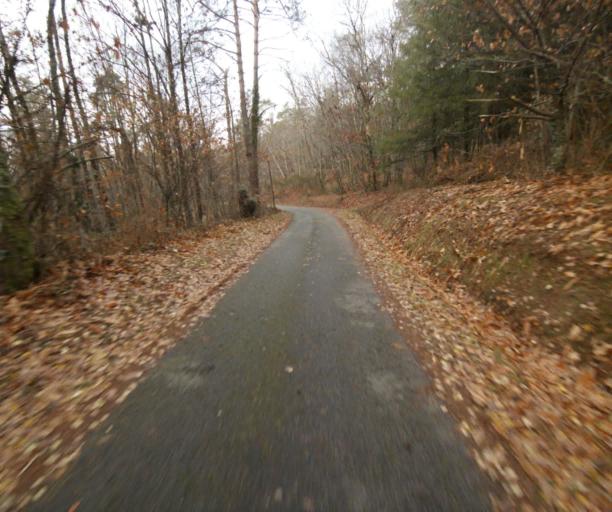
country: FR
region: Limousin
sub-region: Departement de la Correze
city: Chameyrat
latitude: 45.2231
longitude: 1.6988
